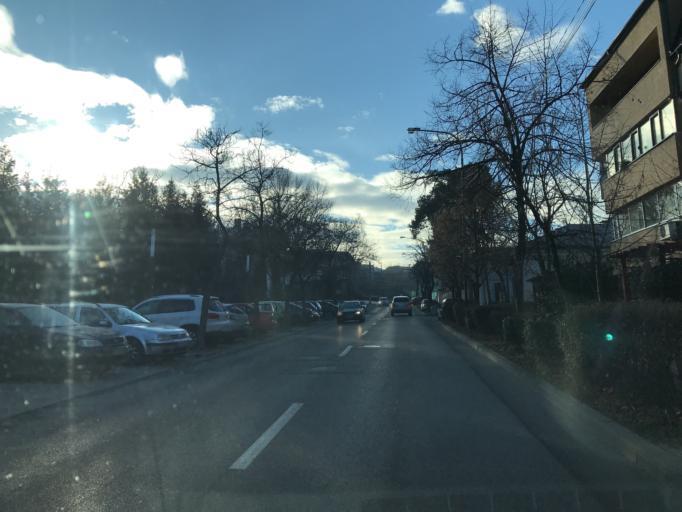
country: RO
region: Olt
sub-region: Municipiul Slatina
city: Slatina
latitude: 44.4297
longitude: 24.3611
